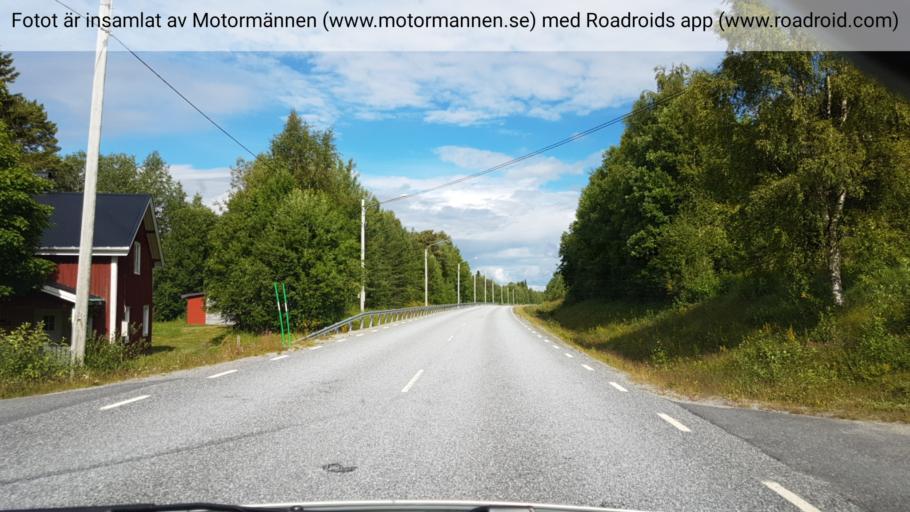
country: SE
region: Vaesterbotten
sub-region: Vilhelmina Kommun
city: Vilhelmina
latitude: 64.4188
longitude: 16.8079
